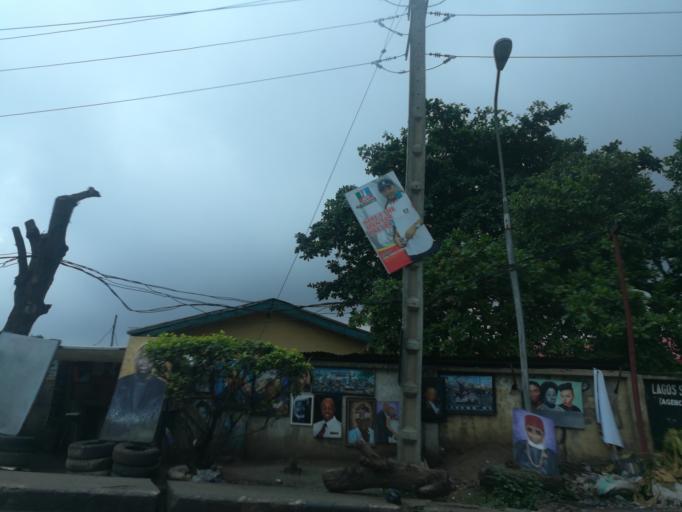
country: NG
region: Lagos
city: Agege
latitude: 6.6167
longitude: 3.3353
